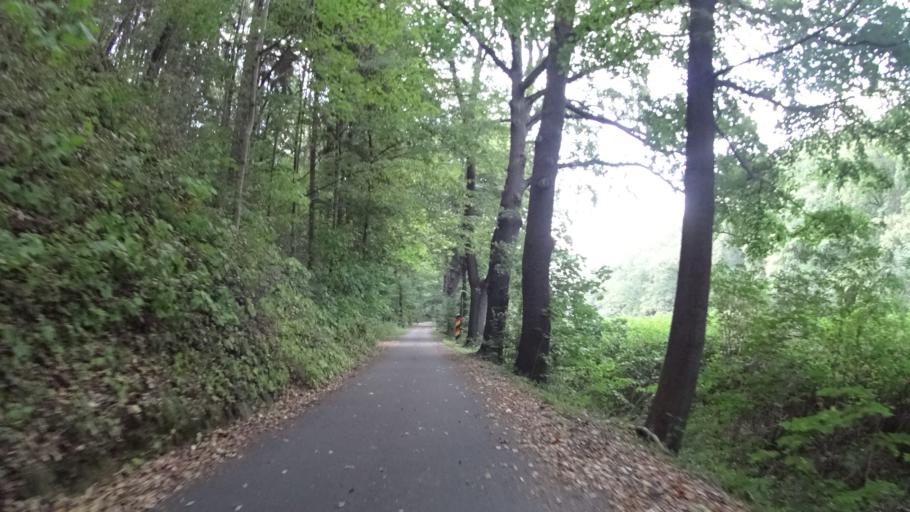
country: DE
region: Saxony
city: Ostritz
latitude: 50.9921
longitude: 14.9167
